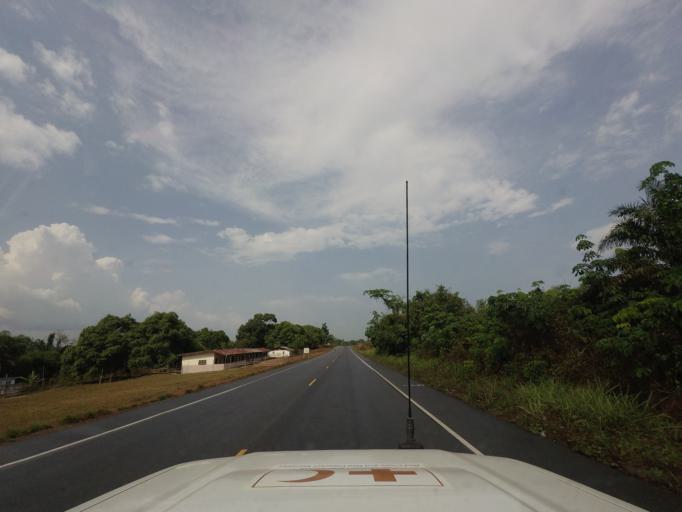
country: LR
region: Margibi
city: Kakata
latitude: 6.6207
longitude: -10.2602
